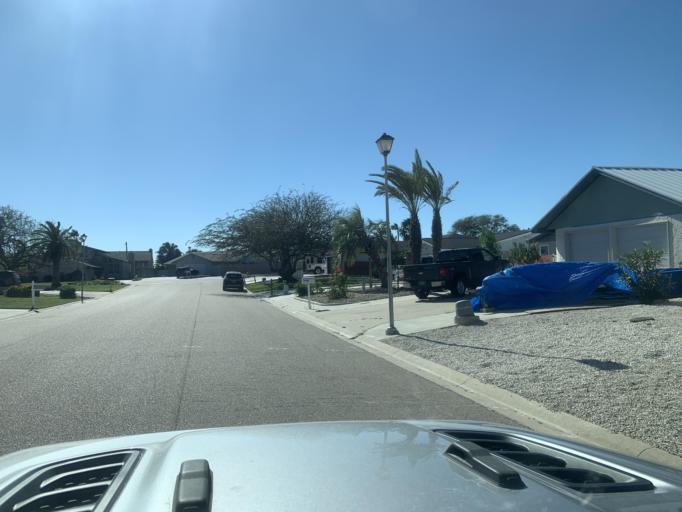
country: US
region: Texas
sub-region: Nueces County
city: Corpus Christi
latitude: 27.6256
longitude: -97.2278
